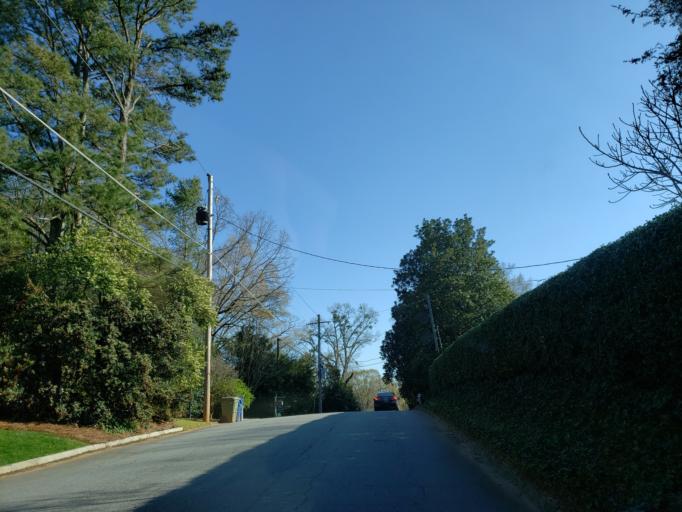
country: US
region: Georgia
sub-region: DeKalb County
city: North Atlanta
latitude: 33.8470
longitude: -84.3976
